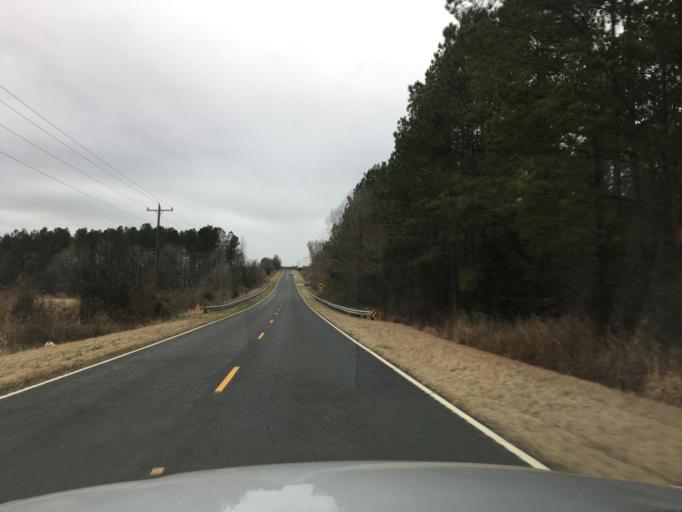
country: US
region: South Carolina
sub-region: Greenwood County
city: Greenwood
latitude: 34.1198
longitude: -82.1711
